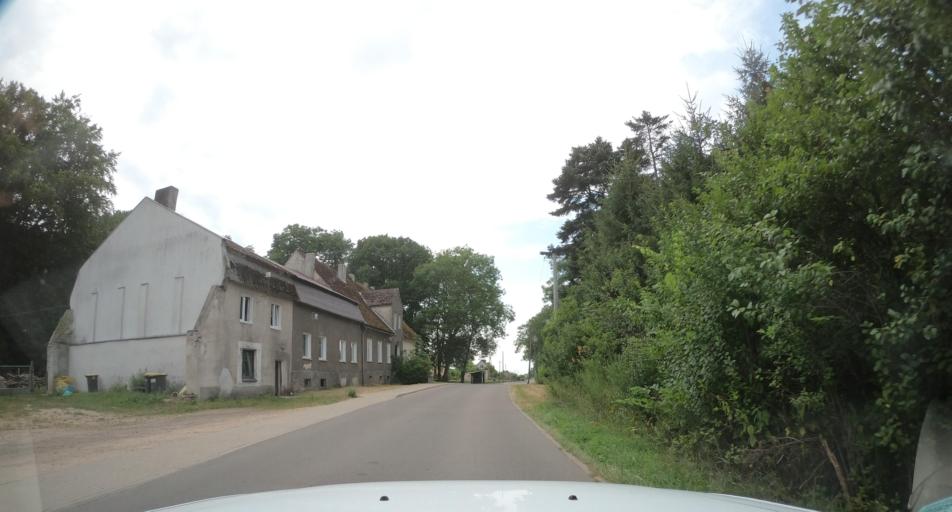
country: PL
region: West Pomeranian Voivodeship
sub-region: Powiat walecki
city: Tuczno
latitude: 53.2317
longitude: 16.2454
